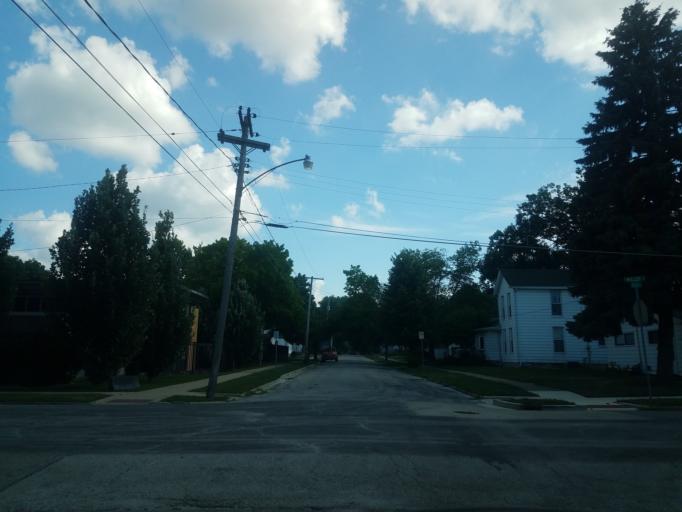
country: US
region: Illinois
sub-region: McLean County
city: Bloomington
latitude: 40.4698
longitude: -88.9911
